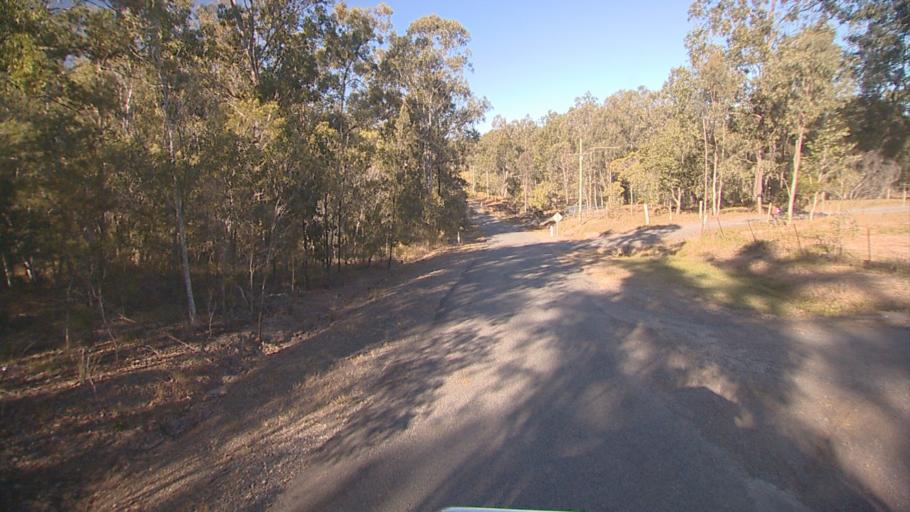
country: AU
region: Queensland
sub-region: Ipswich
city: Springfield Lakes
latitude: -27.6884
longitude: 152.9300
